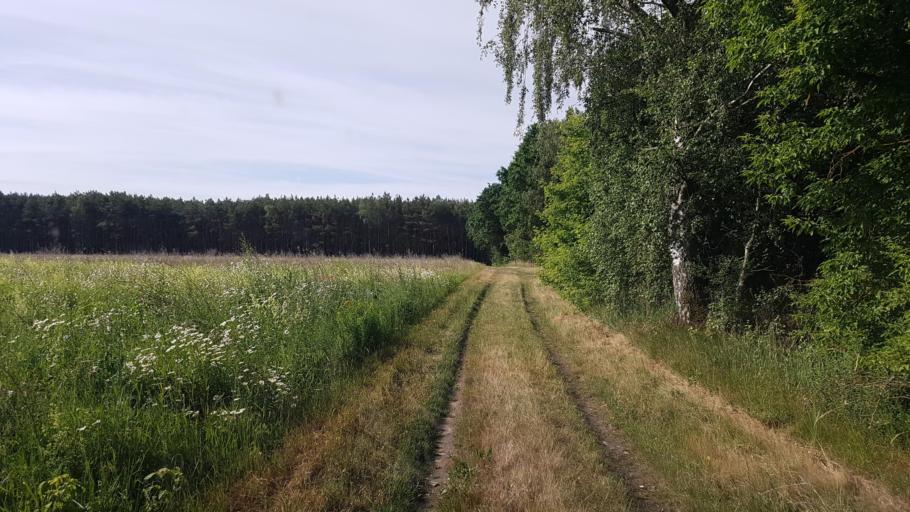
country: DE
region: Brandenburg
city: Plessa
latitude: 51.5313
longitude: 13.6503
